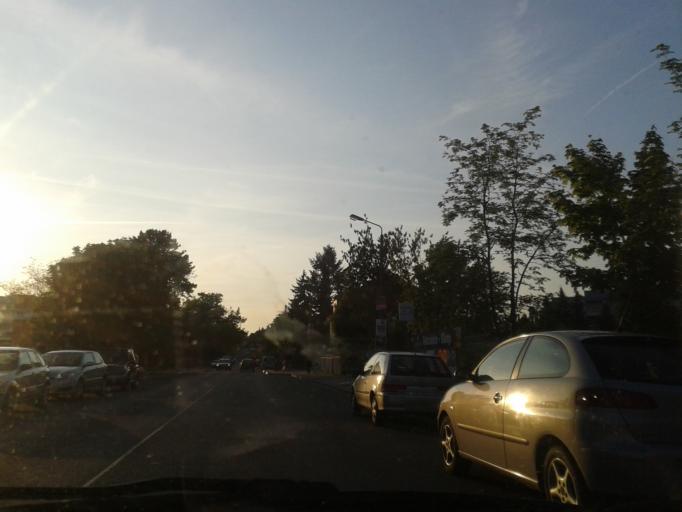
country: DE
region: Saxony
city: Dresden
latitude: 51.0169
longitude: 13.7620
